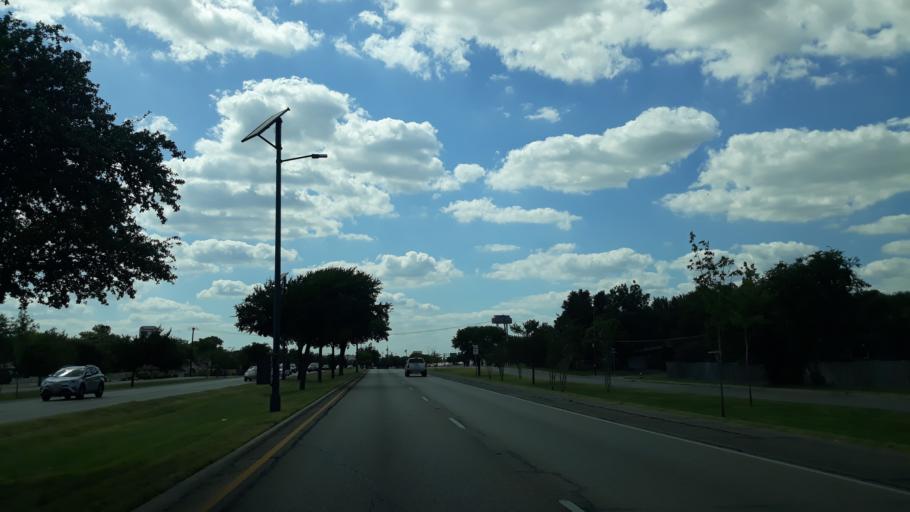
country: US
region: Texas
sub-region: Dallas County
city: Irving
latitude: 32.8312
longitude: -96.9835
